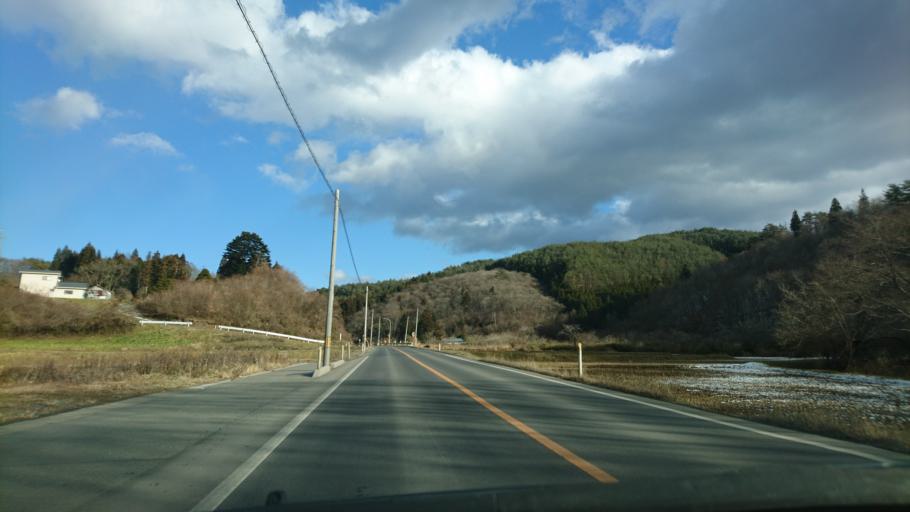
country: JP
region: Iwate
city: Ichinoseki
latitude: 38.7849
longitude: 141.3989
